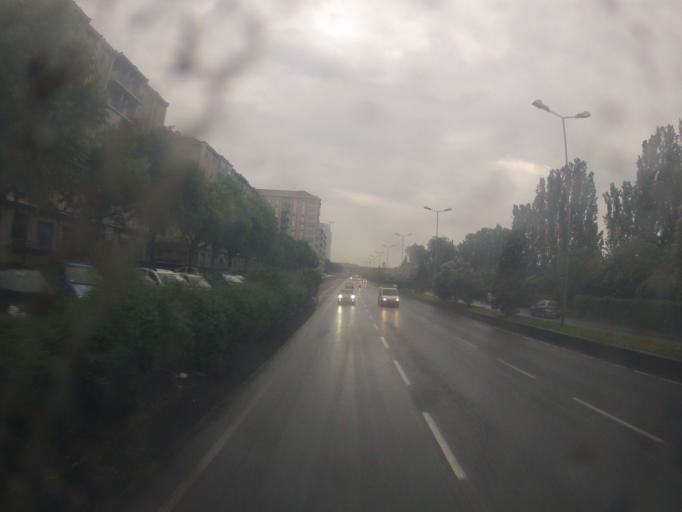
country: IT
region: Piedmont
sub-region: Provincia di Torino
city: Moncalieri
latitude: 45.0108
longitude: 7.6705
